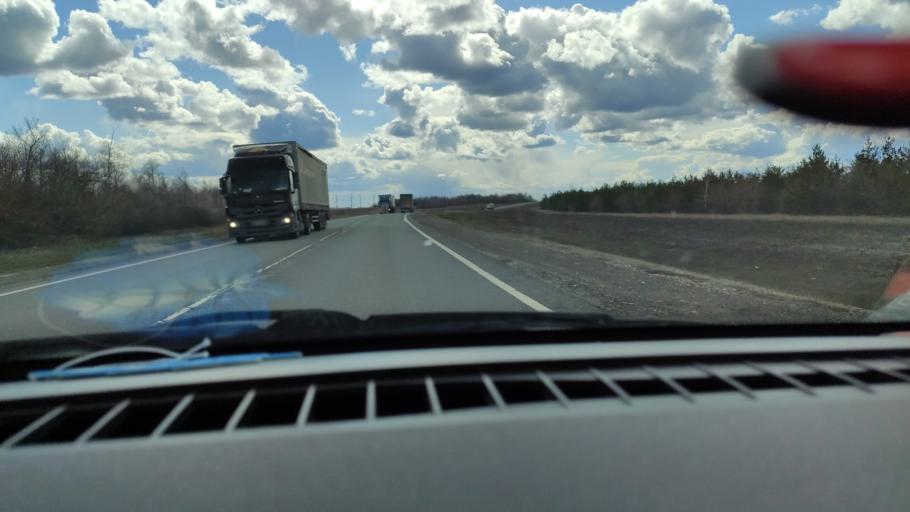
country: RU
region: Samara
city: Syzran'
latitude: 52.8674
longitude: 48.2777
